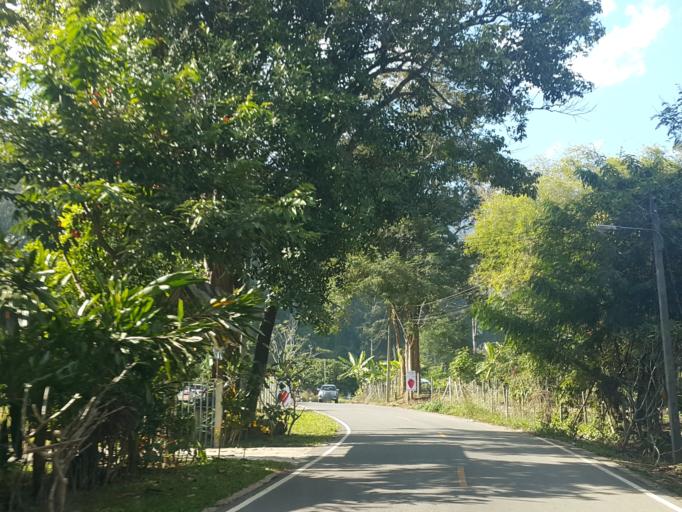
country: TH
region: Chiang Mai
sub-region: Amphoe Chiang Dao
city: Chiang Dao
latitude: 19.4063
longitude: 98.9260
